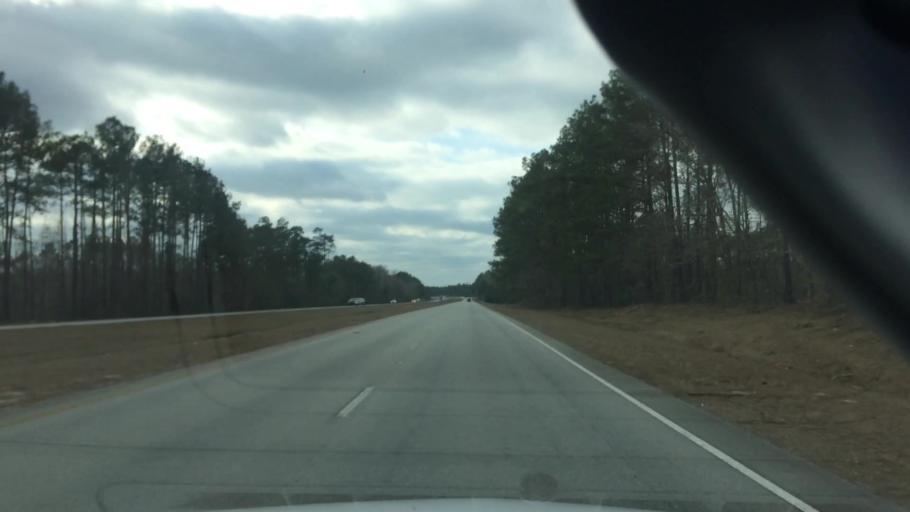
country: US
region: North Carolina
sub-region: Brunswick County
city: Bolivia
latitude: 34.0658
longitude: -78.1875
